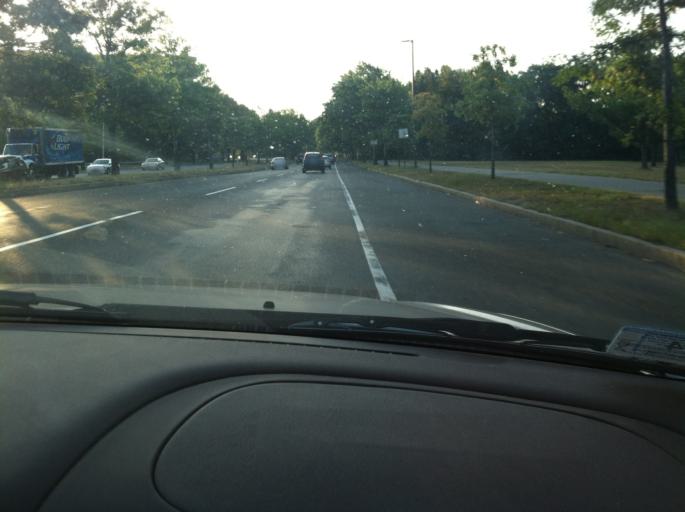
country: US
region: Massachusetts
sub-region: Middlesex County
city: Medford
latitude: 42.4120
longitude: -71.1050
